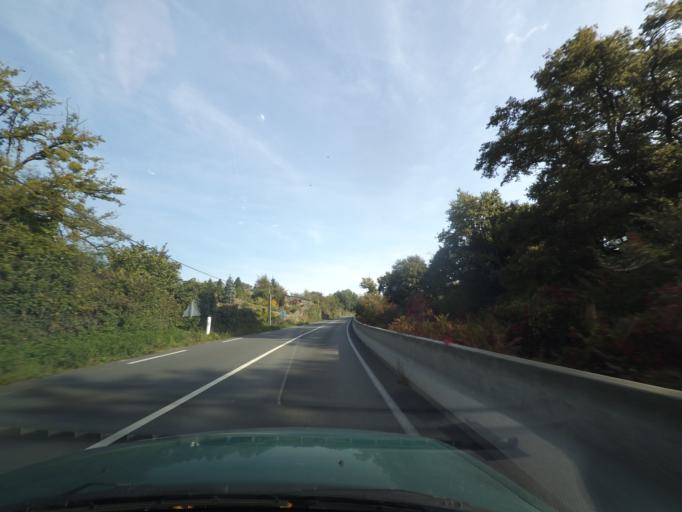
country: FR
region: Pays de la Loire
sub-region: Departement de la Vendee
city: Tiffauges
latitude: 47.0184
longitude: -1.1086
